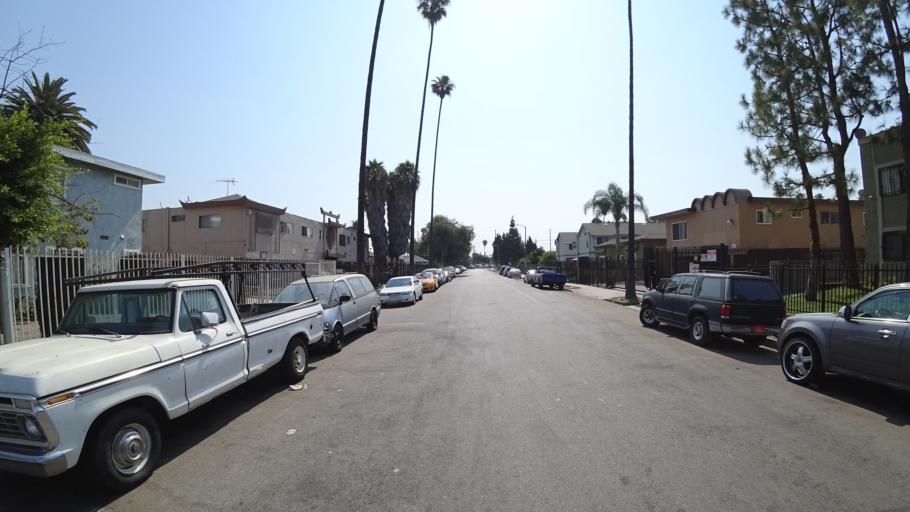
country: US
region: California
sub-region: Los Angeles County
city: Westmont
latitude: 33.9655
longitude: -118.2848
